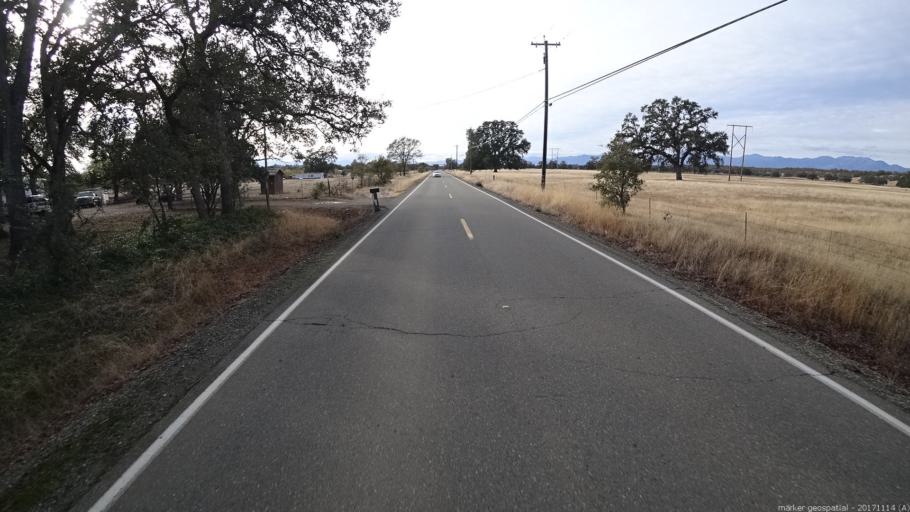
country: US
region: California
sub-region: Shasta County
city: Anderson
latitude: 40.3883
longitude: -122.4554
